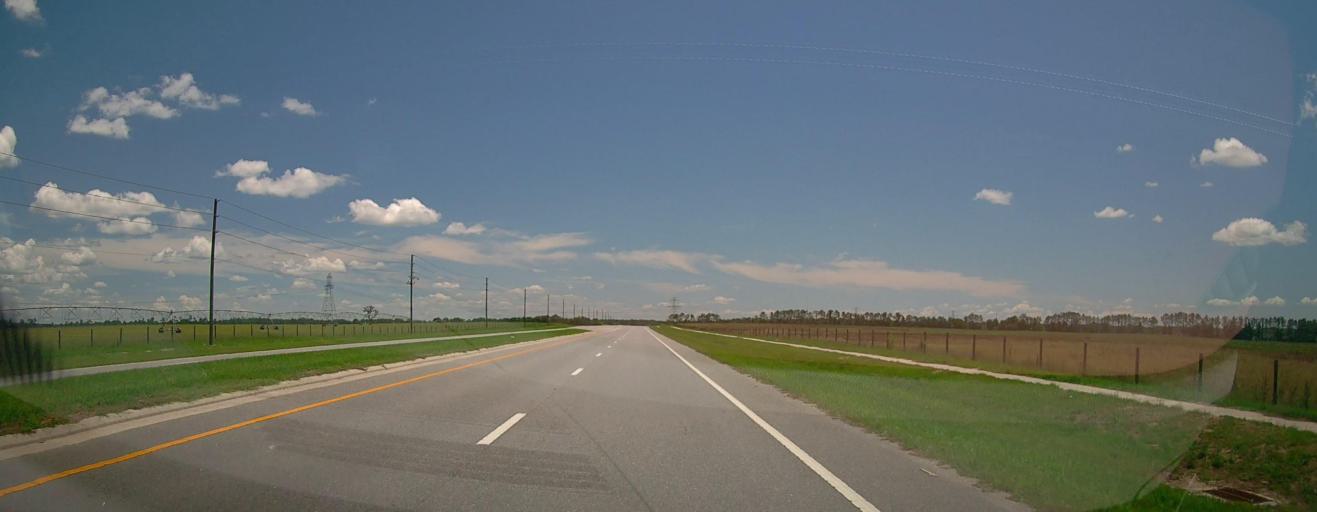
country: US
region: Florida
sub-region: Marion County
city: Silver Springs Shores
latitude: 29.0749
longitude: -82.0308
